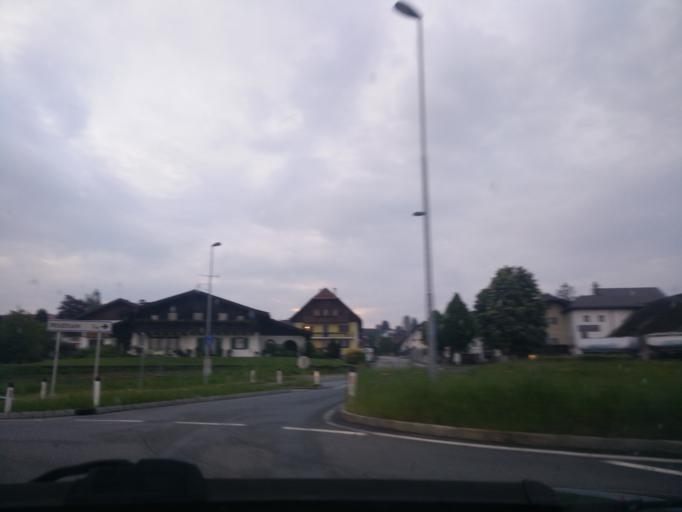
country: AT
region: Salzburg
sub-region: Politischer Bezirk Salzburg-Umgebung
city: Seekirchen am Wallersee
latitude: 47.8969
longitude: 13.1187
